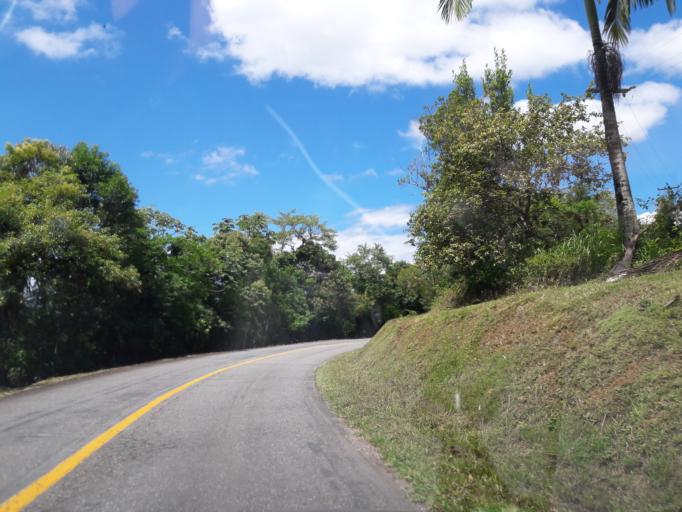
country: BR
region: Parana
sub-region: Antonina
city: Antonina
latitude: -25.4299
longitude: -48.8055
